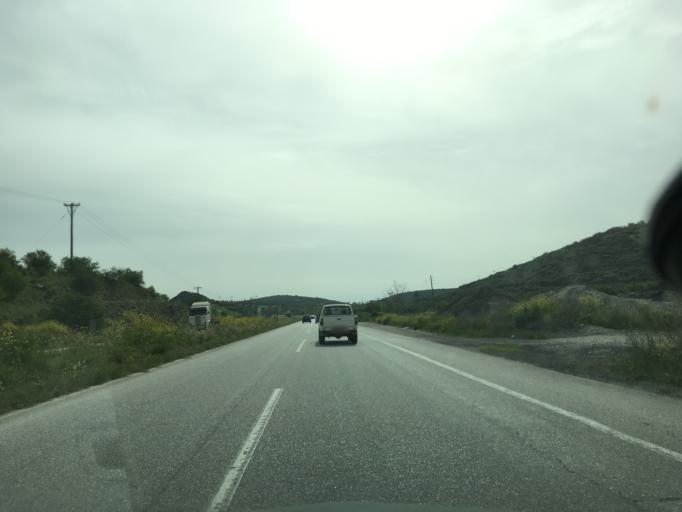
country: GR
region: Thessaly
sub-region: Nomos Magnisias
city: Velestino
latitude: 39.3834
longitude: 22.8212
